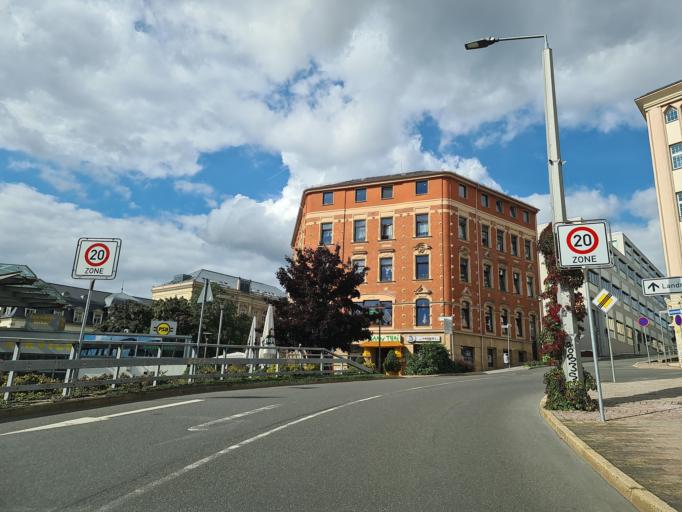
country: DE
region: Saxony
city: Plauen
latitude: 50.4965
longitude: 12.1370
